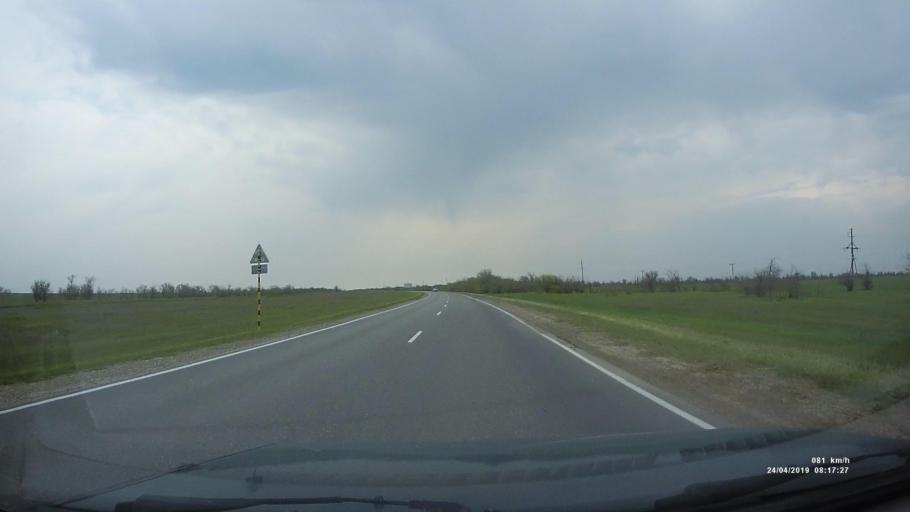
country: RU
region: Kalmykiya
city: Priyutnoye
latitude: 46.0979
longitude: 43.6302
